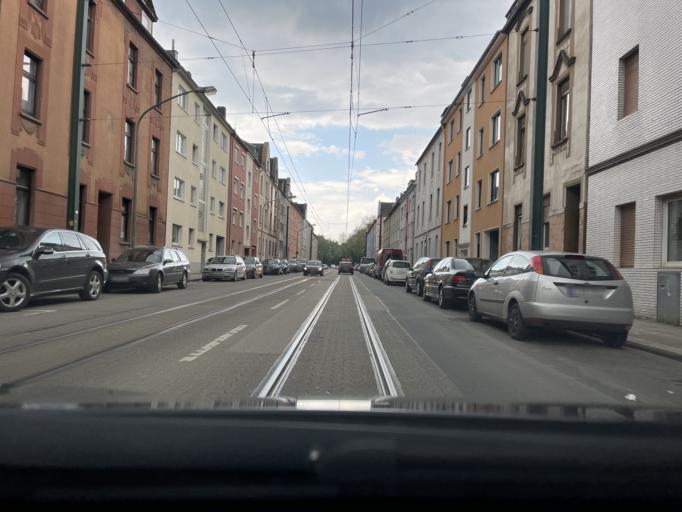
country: DE
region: North Rhine-Westphalia
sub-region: Regierungsbezirk Dusseldorf
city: Essen
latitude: 51.4691
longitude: 6.9792
